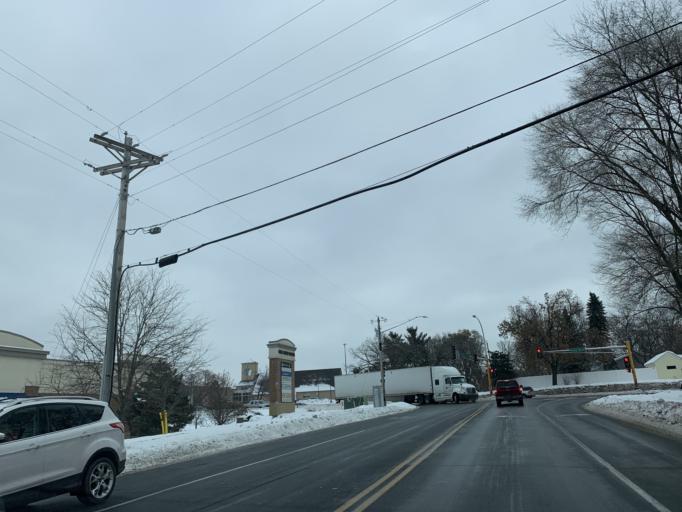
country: US
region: Minnesota
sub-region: Anoka County
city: Coon Rapids
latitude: 45.1498
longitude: -93.2768
